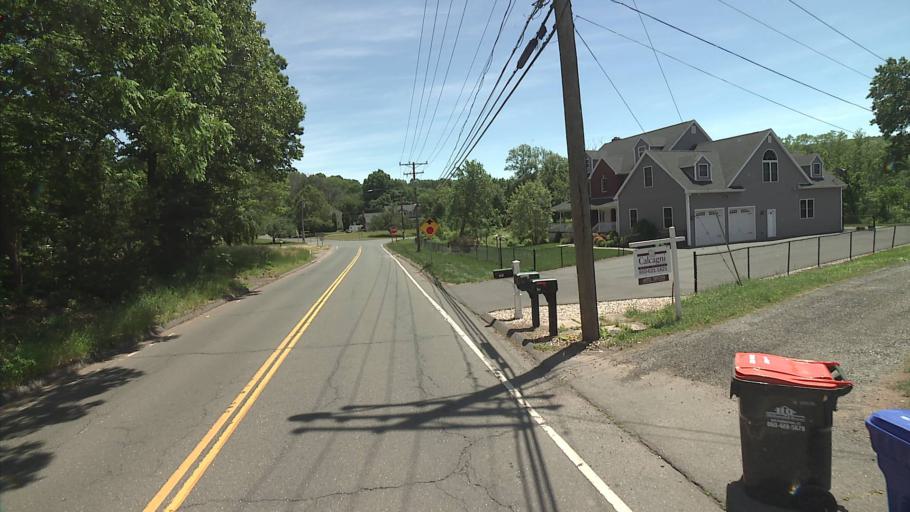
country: US
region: Connecticut
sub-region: New Haven County
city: Meriden
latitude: 41.5968
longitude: -72.8440
